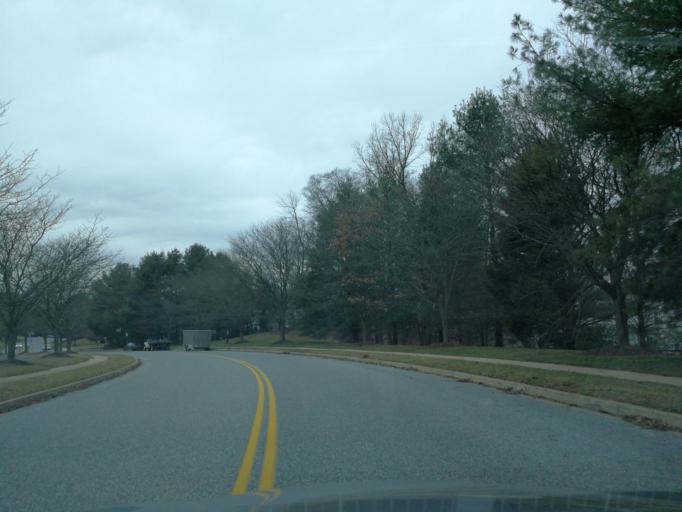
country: US
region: Maryland
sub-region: Harford County
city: Bel Air South
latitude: 39.4752
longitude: -76.3213
